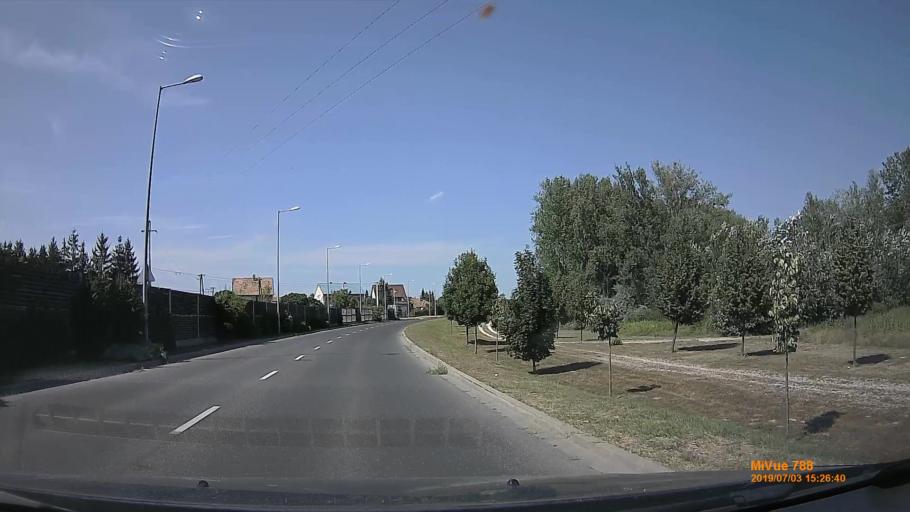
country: HU
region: Gyor-Moson-Sopron
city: Gyor
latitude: 47.7141
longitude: 17.6536
